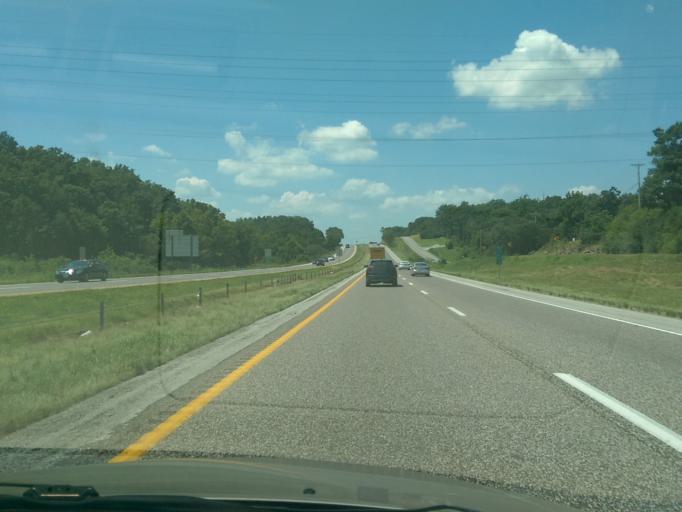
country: US
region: Missouri
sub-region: Boone County
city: Columbia
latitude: 38.9692
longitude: -92.3779
